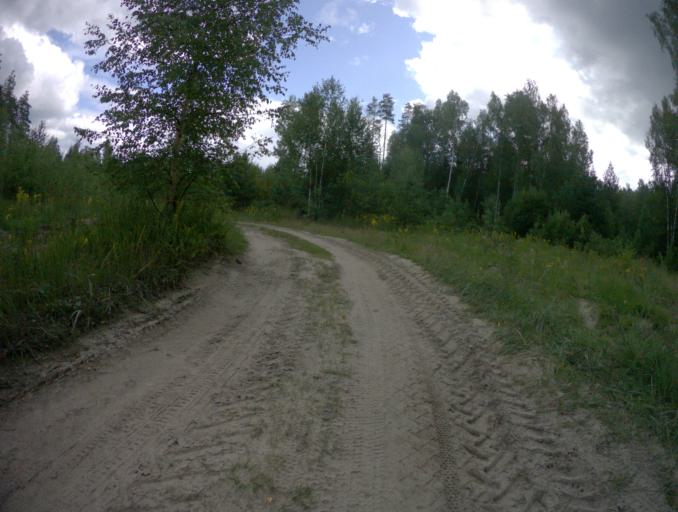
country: RU
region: Vladimir
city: Vorsha
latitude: 55.9522
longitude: 40.1464
